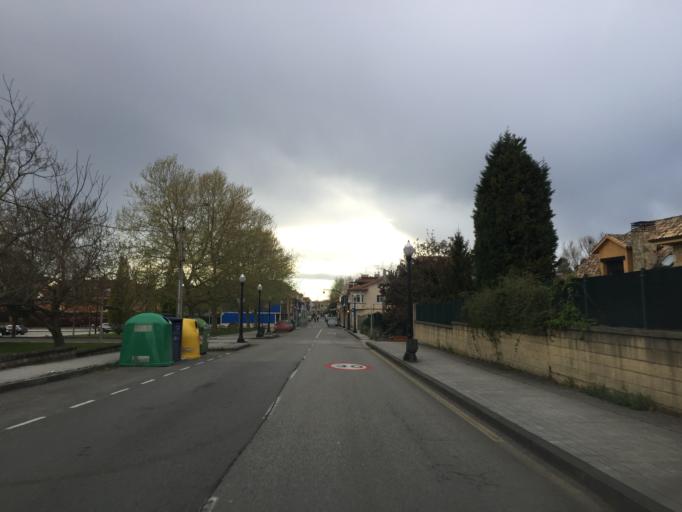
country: ES
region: Asturias
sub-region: Province of Asturias
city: Gijon
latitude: 43.5306
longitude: -5.6319
